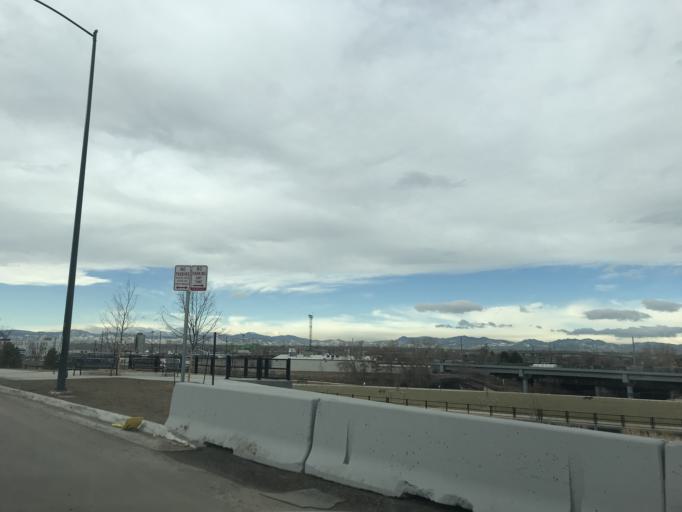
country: US
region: Colorado
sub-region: Denver County
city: Denver
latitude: 39.7769
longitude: -104.9755
